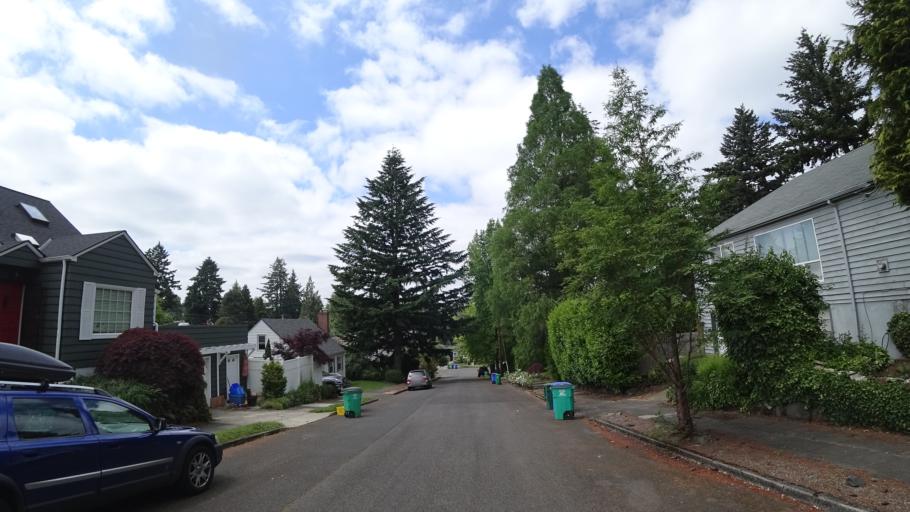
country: US
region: Oregon
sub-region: Clackamas County
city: Lake Oswego
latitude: 45.4662
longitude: -122.6888
